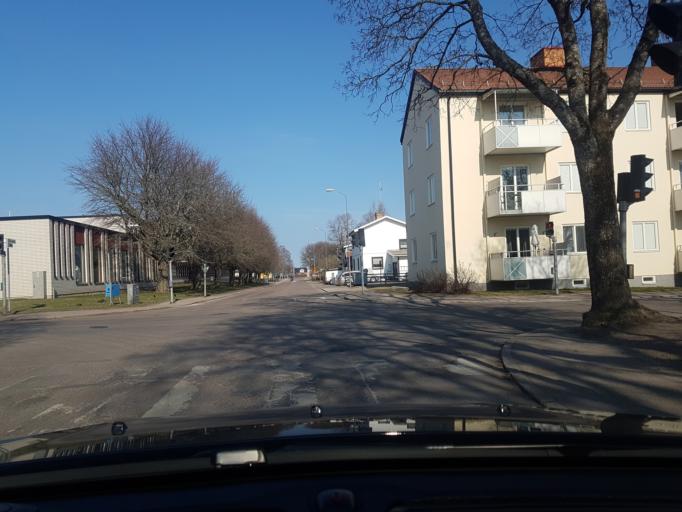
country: SE
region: Dalarna
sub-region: Borlange Kommun
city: Borlaenge
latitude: 60.4927
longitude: 15.4172
